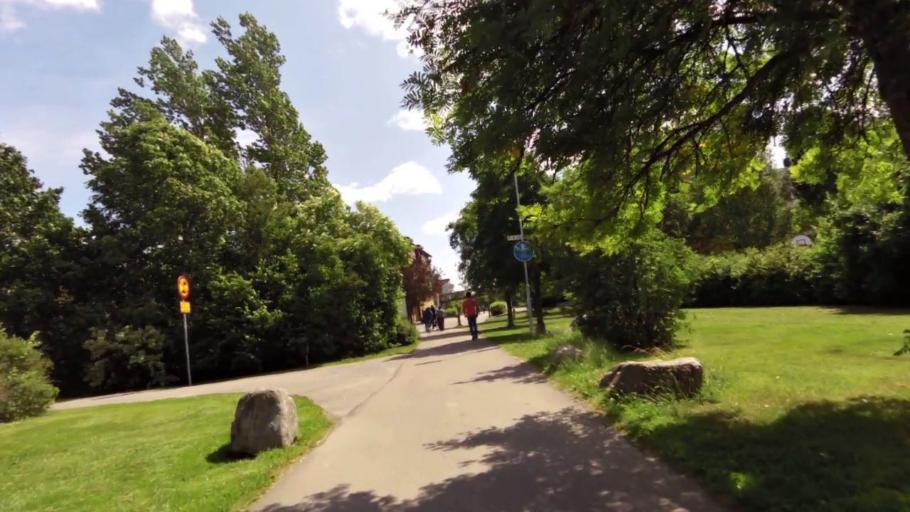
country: SE
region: OEstergoetland
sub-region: Linkopings Kommun
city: Linkoping
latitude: 58.4283
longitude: 15.5818
